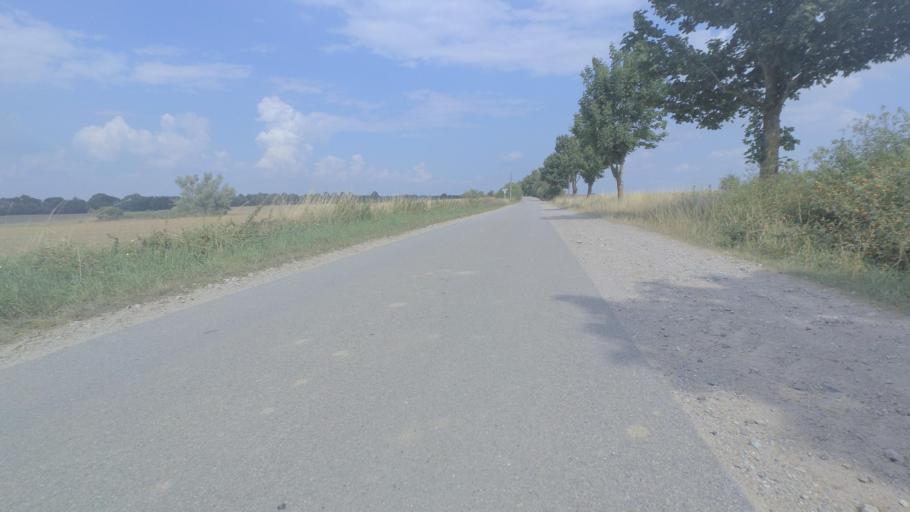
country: DE
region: Mecklenburg-Vorpommern
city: Borrentin
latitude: 53.8219
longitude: 12.9272
